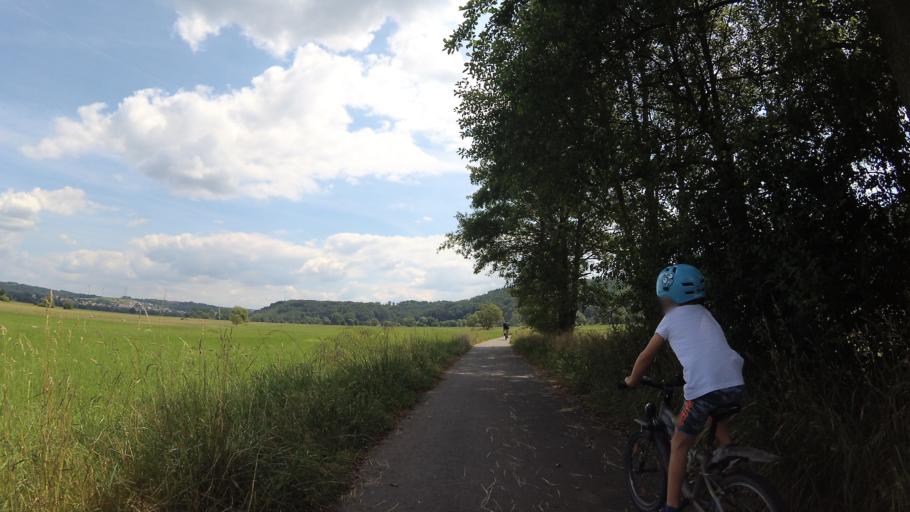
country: DE
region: Saarland
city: Blieskastel
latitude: 49.2614
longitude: 7.2902
